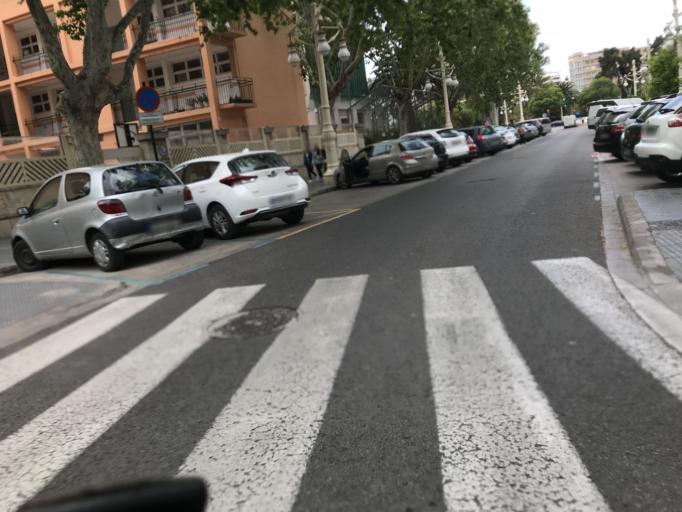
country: ES
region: Valencia
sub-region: Provincia de Valencia
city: Valencia
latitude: 39.4729
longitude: -0.3620
